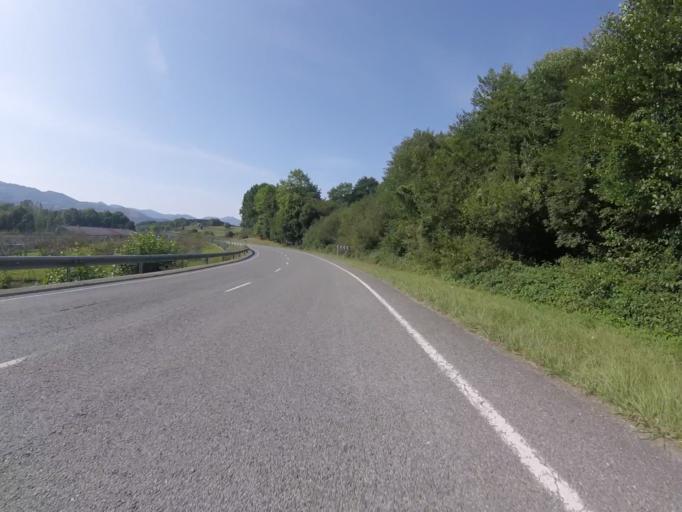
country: ES
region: Navarre
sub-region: Provincia de Navarra
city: Zugarramurdi
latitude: 43.1932
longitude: -1.4858
